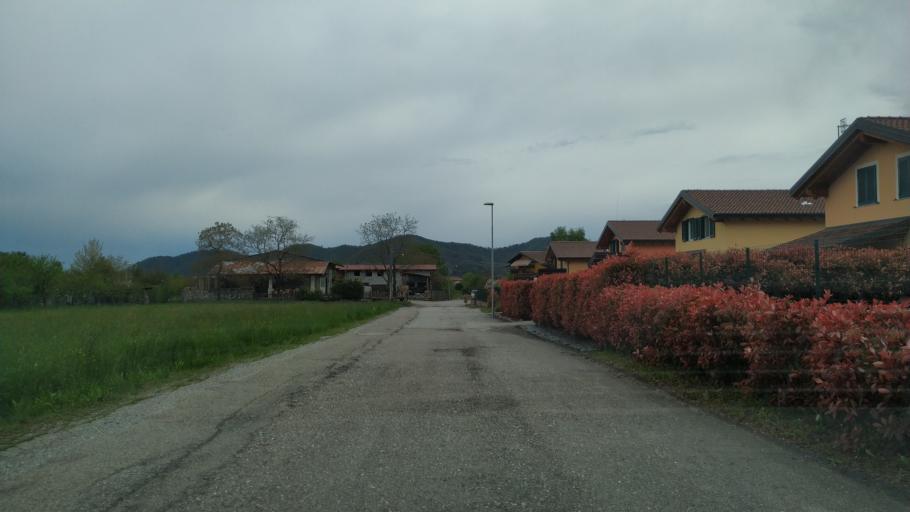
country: IT
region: Piedmont
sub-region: Provincia di Novara
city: Grignasco
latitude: 45.6792
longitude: 8.3469
